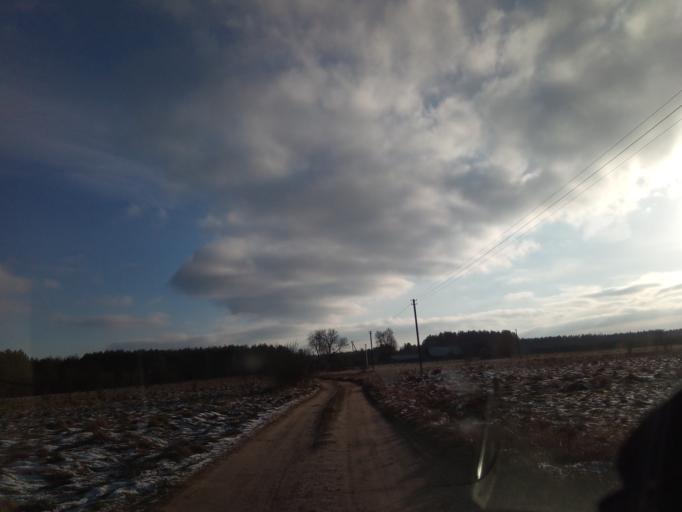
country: LT
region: Alytaus apskritis
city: Druskininkai
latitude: 53.9789
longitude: 24.2418
